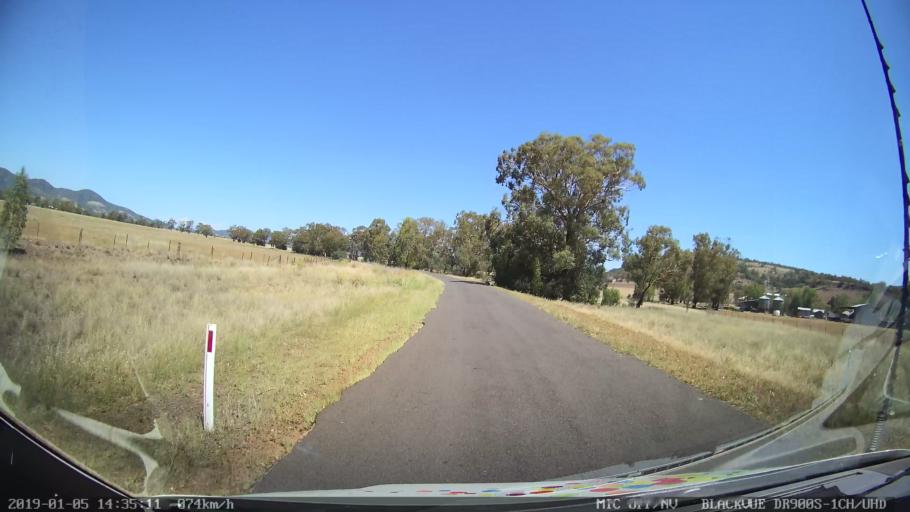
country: AU
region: New South Wales
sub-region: Tamworth Municipality
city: Phillip
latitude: -31.2394
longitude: 150.6476
